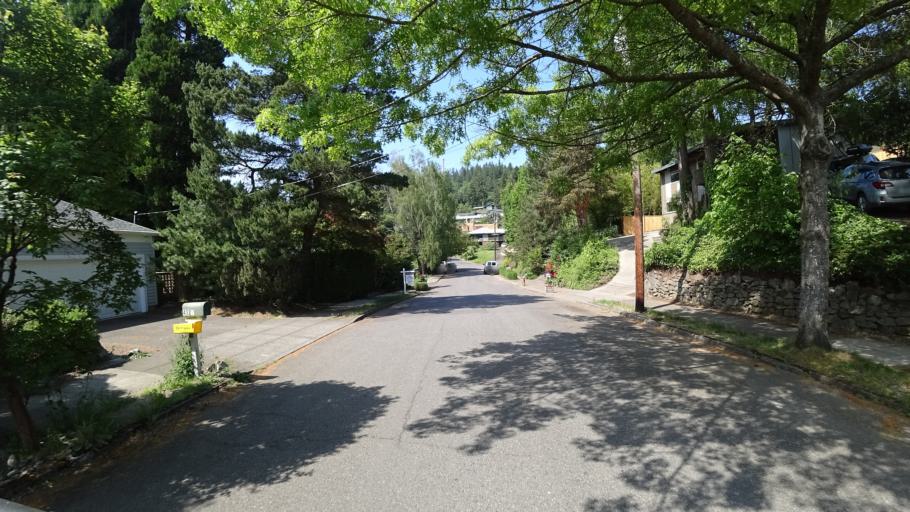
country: US
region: Oregon
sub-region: Multnomah County
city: Portland
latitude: 45.4920
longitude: -122.7084
